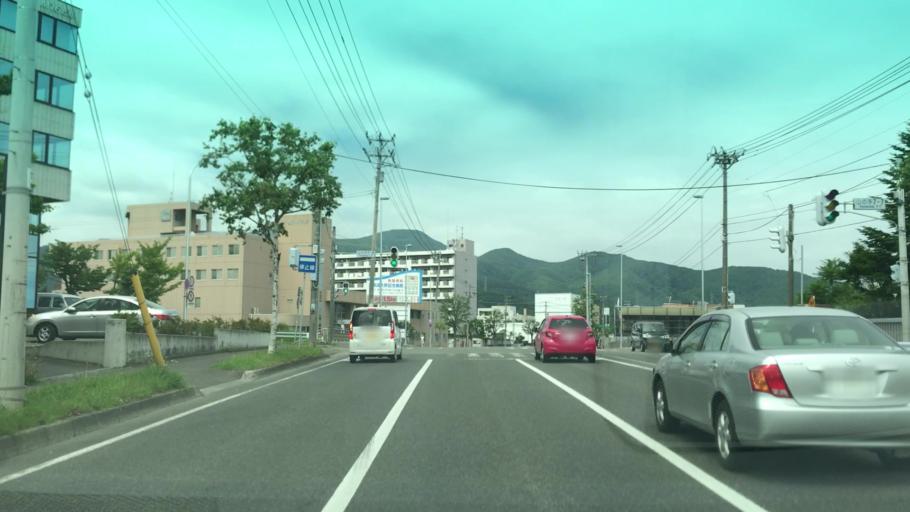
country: JP
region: Hokkaido
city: Sapporo
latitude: 43.0712
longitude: 141.2848
